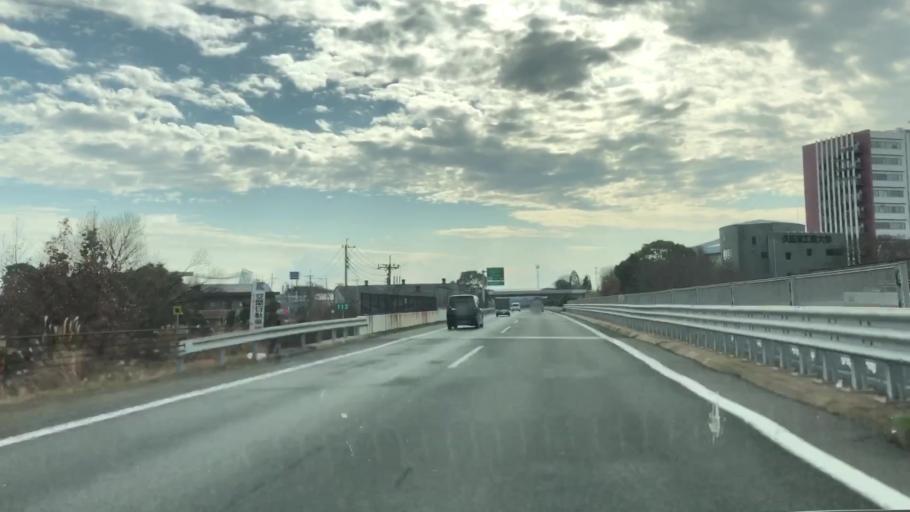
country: JP
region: Fukuoka
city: Kurume
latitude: 33.2672
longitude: 130.5392
